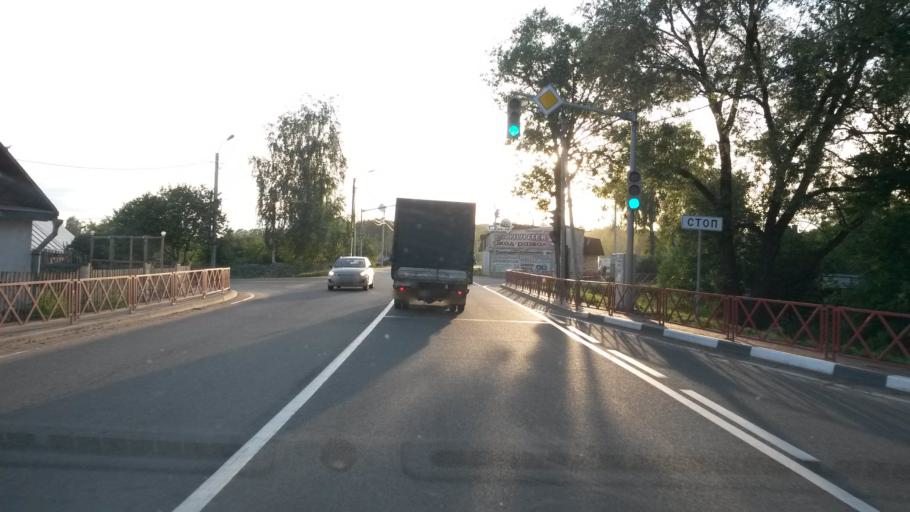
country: RU
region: Jaroslavl
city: Yaroslavl
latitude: 57.7113
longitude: 39.8364
